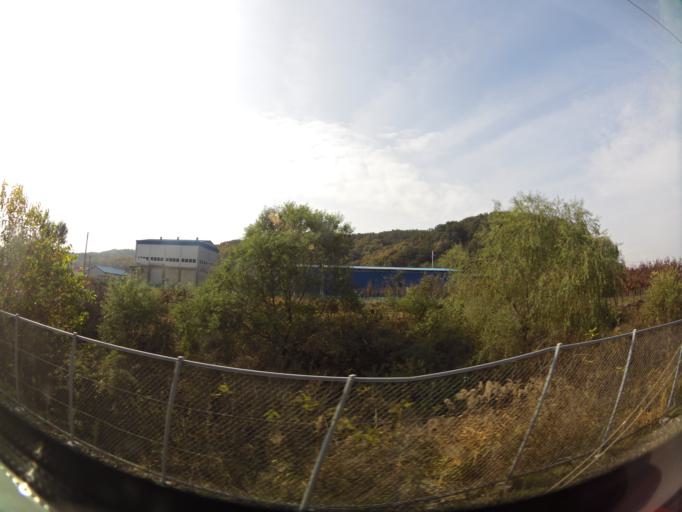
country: KR
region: Chungcheongbuk-do
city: Cheongju-si
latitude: 36.6326
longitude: 127.2891
